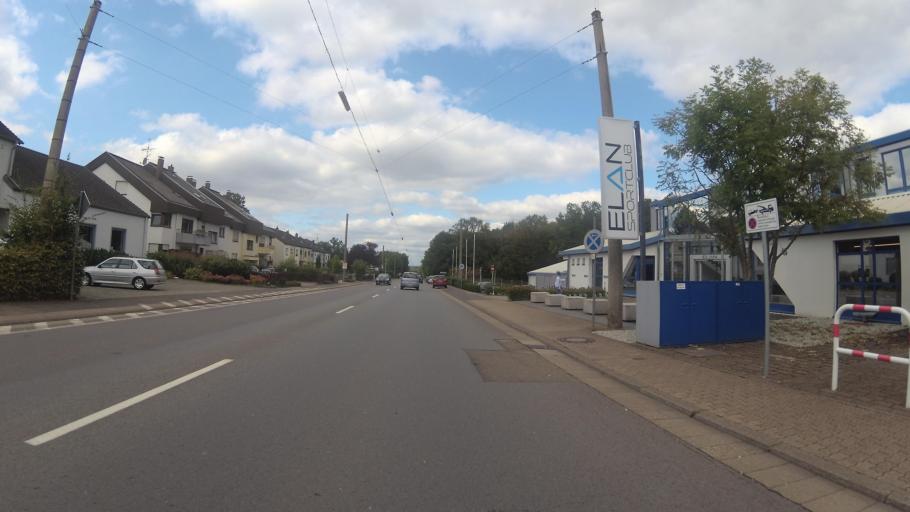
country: DE
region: Saarland
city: Bous
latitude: 49.2611
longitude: 6.8094
